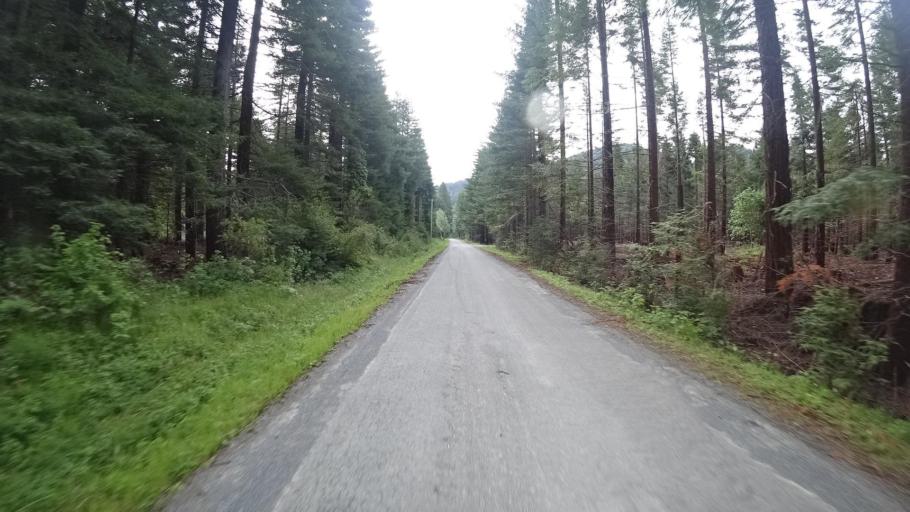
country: US
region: California
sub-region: Humboldt County
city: Redway
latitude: 40.3435
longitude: -123.8838
